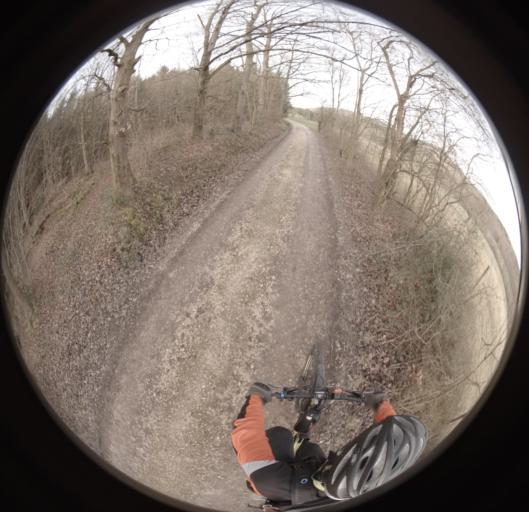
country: DE
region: Baden-Wuerttemberg
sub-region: Regierungsbezirk Stuttgart
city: Ottenbach
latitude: 48.7233
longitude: 9.7312
